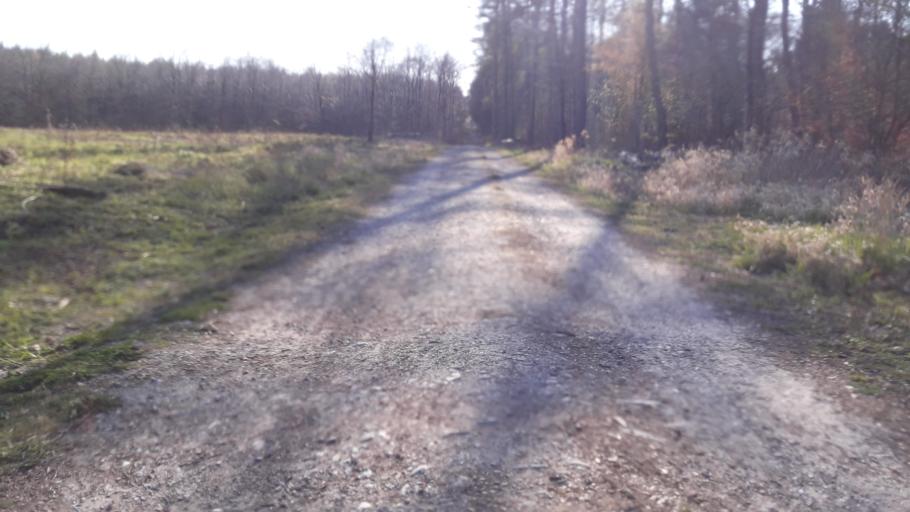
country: DE
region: North Rhine-Westphalia
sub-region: Regierungsbezirk Detmold
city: Salzkotten
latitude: 51.6716
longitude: 8.6690
